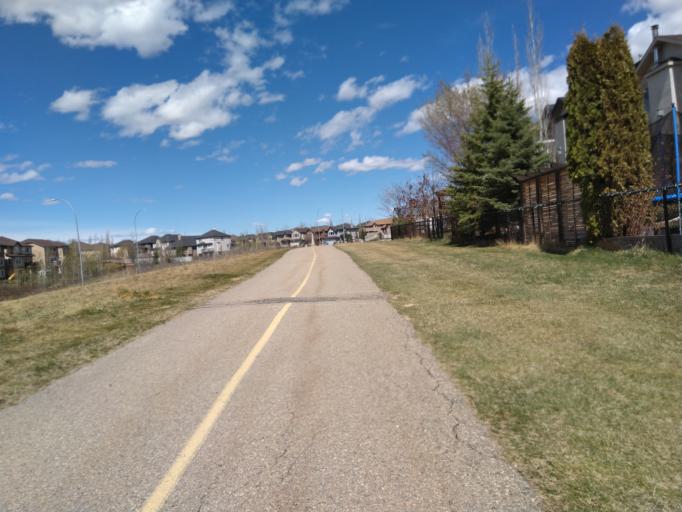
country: CA
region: Alberta
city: Calgary
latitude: 51.1129
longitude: -114.2453
